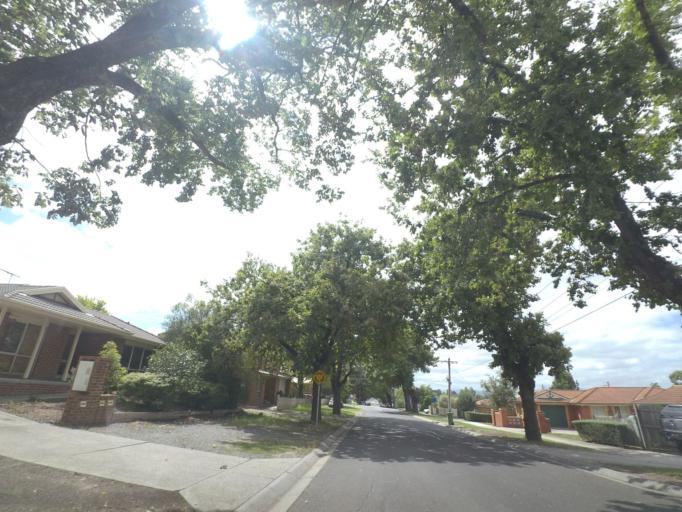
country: AU
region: Victoria
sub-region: Yarra Ranges
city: Lilydale
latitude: -37.7583
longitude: 145.3428
